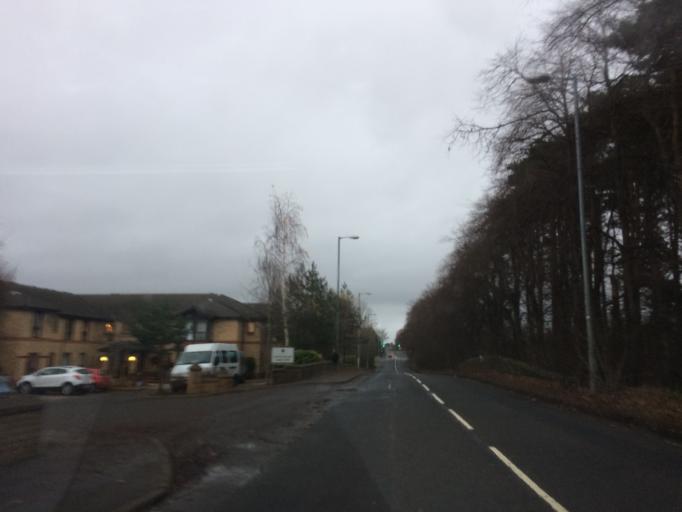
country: GB
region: Scotland
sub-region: East Renfrewshire
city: Newton Mearns
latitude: 55.7966
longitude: -4.3282
